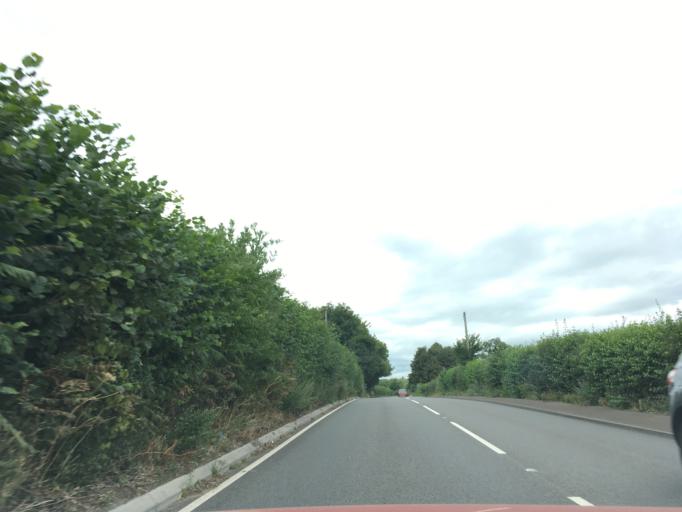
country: GB
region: Wales
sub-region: Monmouthshire
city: Abergavenny
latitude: 51.8016
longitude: -3.0083
